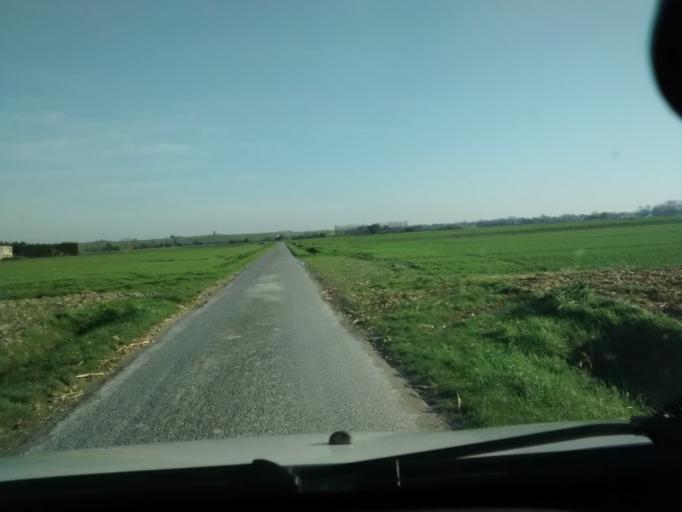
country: FR
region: Lower Normandy
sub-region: Departement de la Manche
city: Pontorson
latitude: 48.5886
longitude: -1.5302
